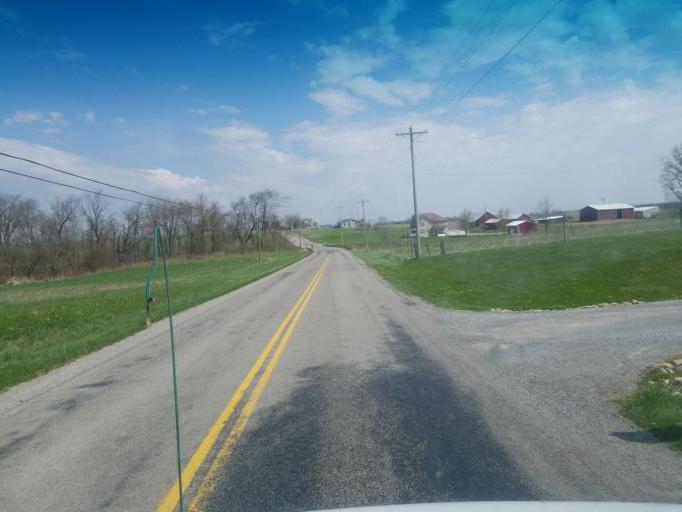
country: US
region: Ohio
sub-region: Hardin County
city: Kenton
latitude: 40.5992
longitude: -83.6716
